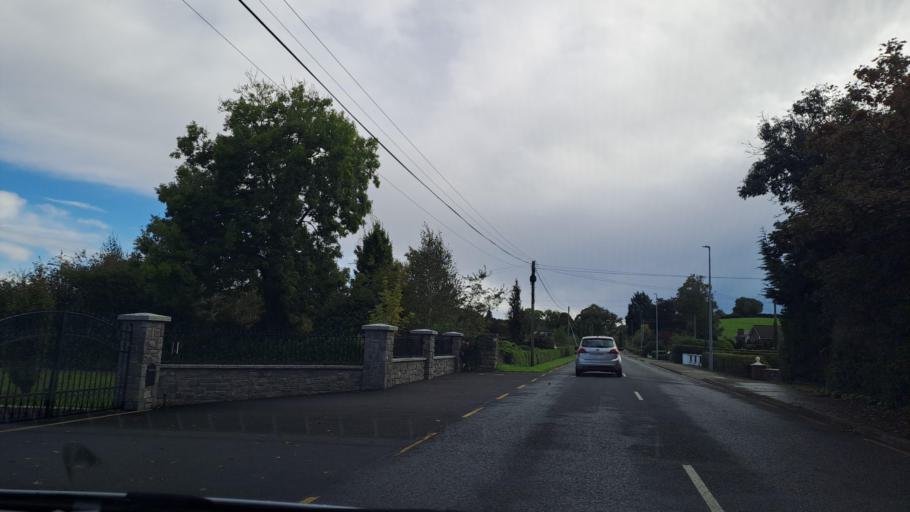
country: IE
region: Ulster
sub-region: County Monaghan
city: Carrickmacross
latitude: 53.9634
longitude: -6.7088
